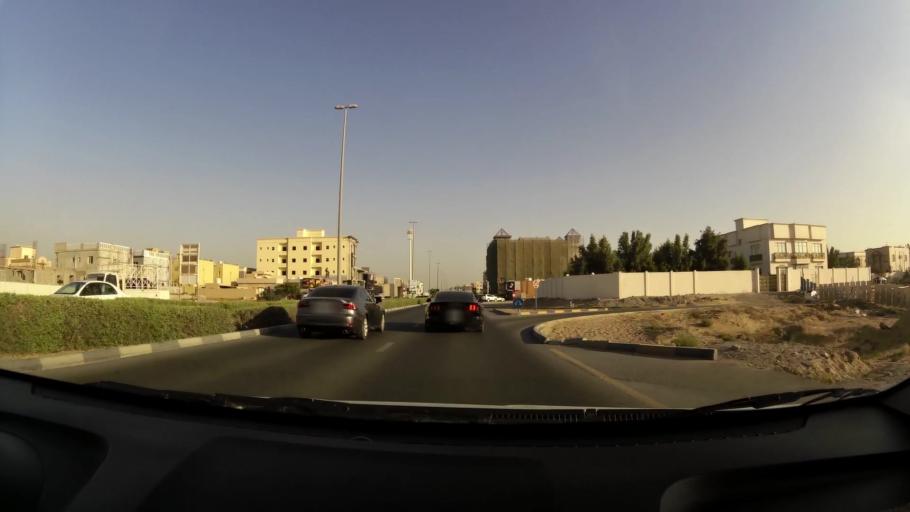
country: AE
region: Ajman
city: Ajman
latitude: 25.3858
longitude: 55.5063
